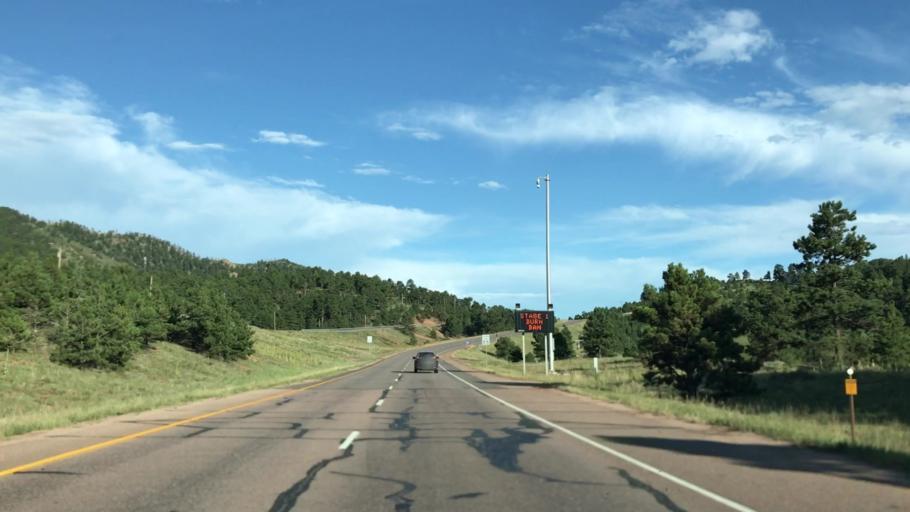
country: US
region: Colorado
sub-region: El Paso County
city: Cascade-Chipita Park
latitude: 38.9405
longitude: -105.0144
